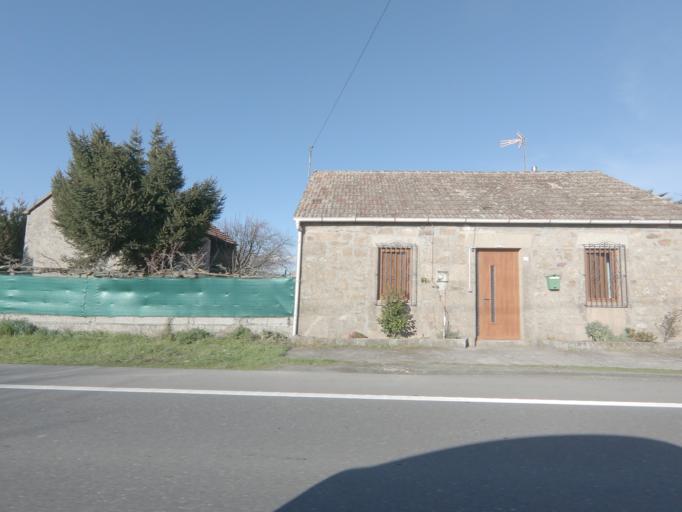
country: ES
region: Galicia
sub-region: Provincia de Pontevedra
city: Silleda
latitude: 42.7220
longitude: -8.2884
